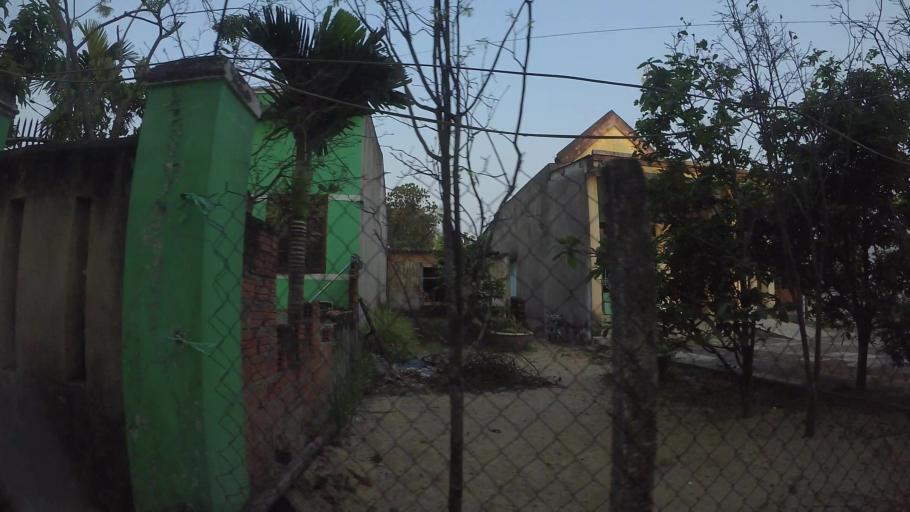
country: VN
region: Da Nang
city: Ngu Hanh Son
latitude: 15.9555
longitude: 108.2536
